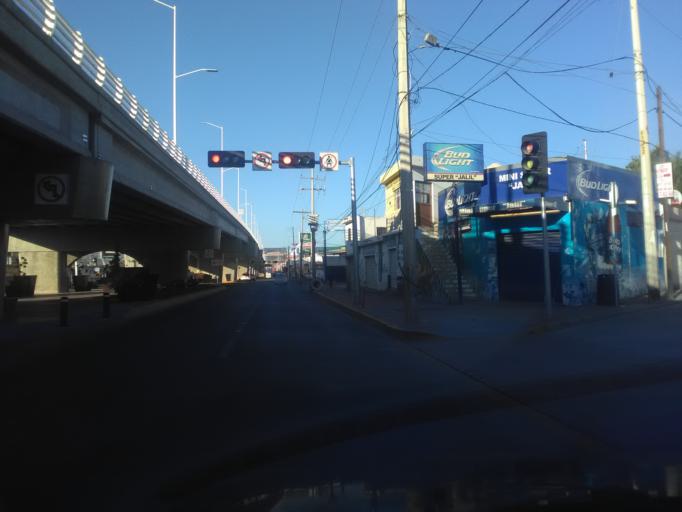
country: MX
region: Durango
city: Victoria de Durango
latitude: 24.0112
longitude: -104.6917
